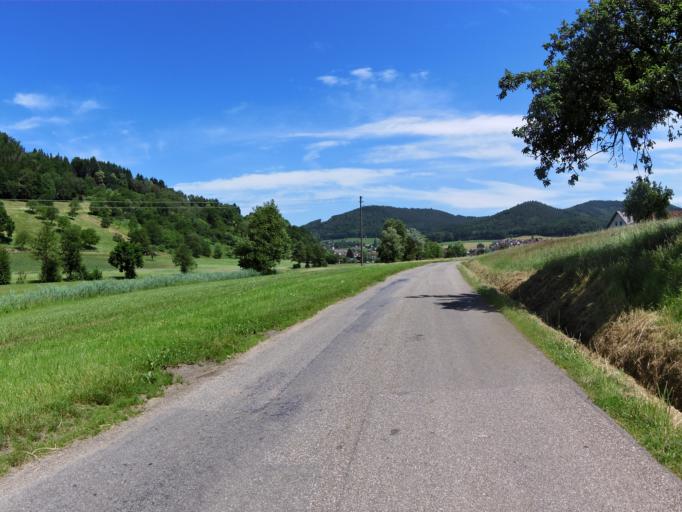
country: DE
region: Baden-Wuerttemberg
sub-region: Freiburg Region
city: Seelbach
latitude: 48.2991
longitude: 7.9285
